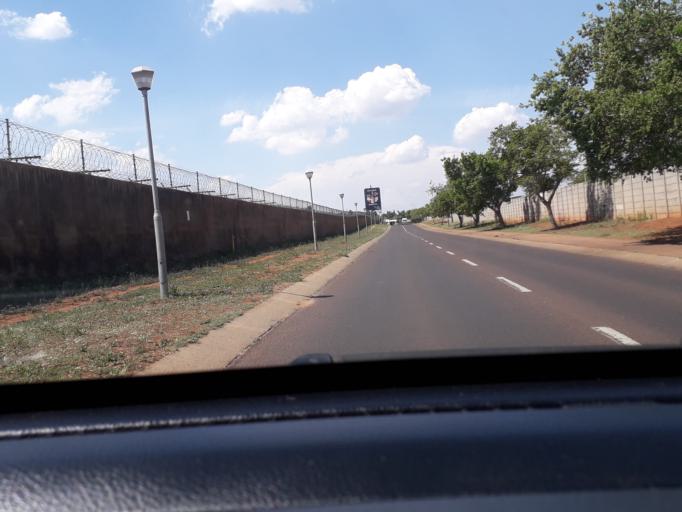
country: ZA
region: Gauteng
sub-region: City of Tshwane Metropolitan Municipality
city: Centurion
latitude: -25.8401
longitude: 28.2323
